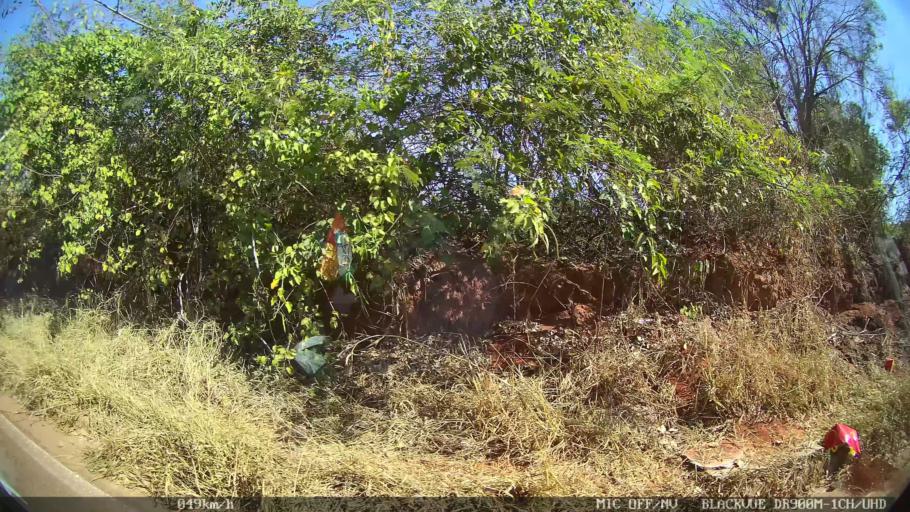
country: BR
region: Sao Paulo
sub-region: Sao Jose Do Rio Preto
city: Sao Jose do Rio Preto
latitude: -20.7610
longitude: -49.4233
